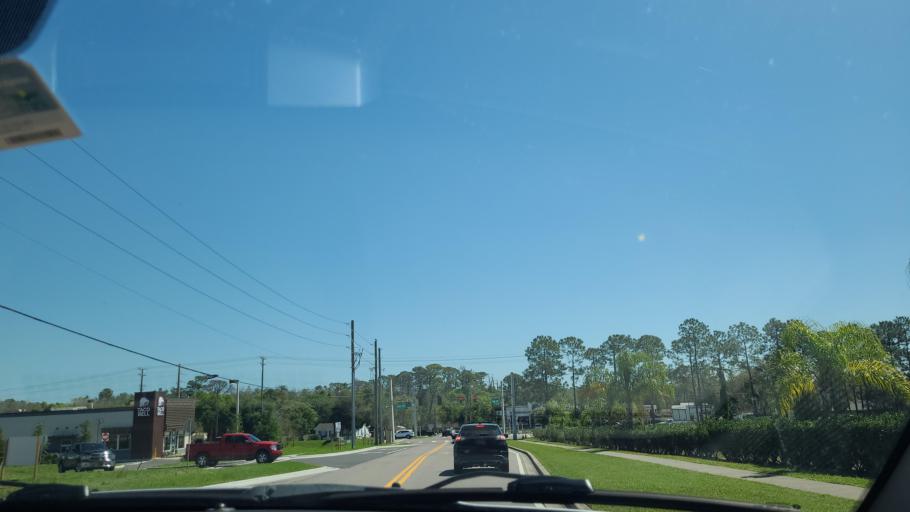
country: US
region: Florida
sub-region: Lake County
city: Tavares
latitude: 28.7822
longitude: -81.7502
